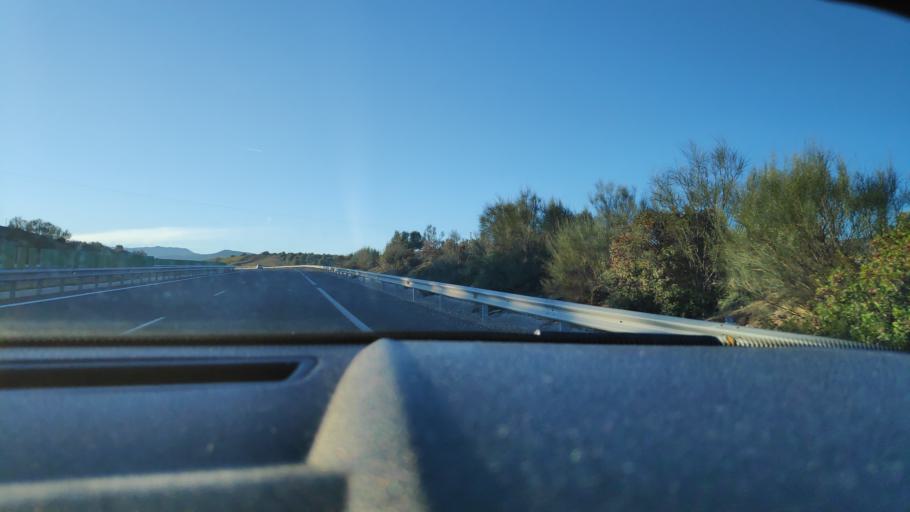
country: ES
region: Andalusia
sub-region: Provincia de Jaen
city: Jaen
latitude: 37.8118
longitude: -3.7349
